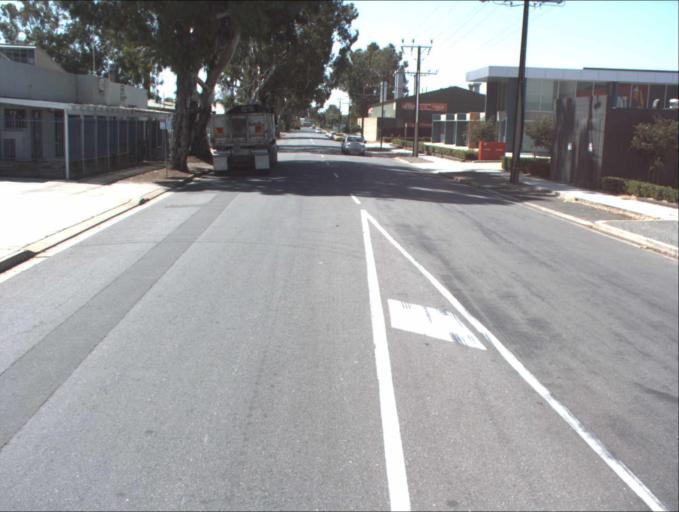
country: AU
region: South Australia
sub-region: Charles Sturt
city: Woodville North
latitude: -34.8497
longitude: 138.5600
